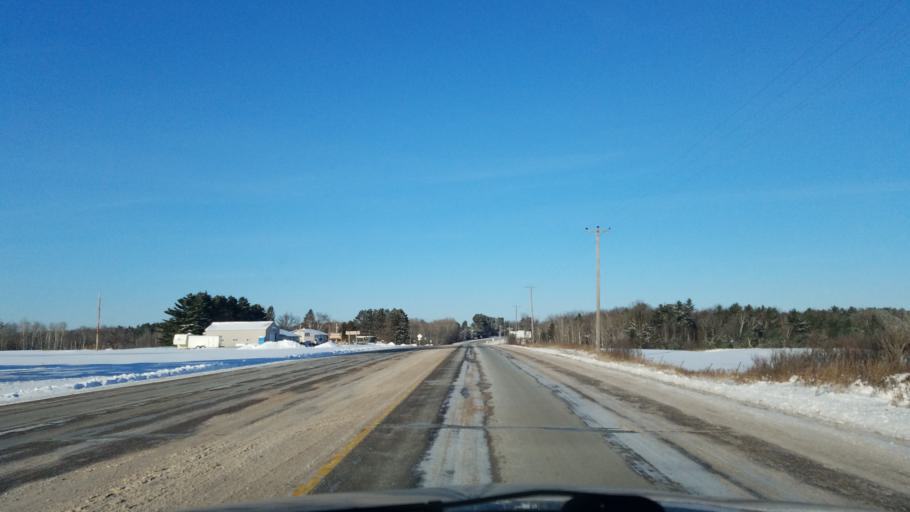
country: US
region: Wisconsin
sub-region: Barron County
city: Cumberland
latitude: 45.5180
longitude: -92.0520
